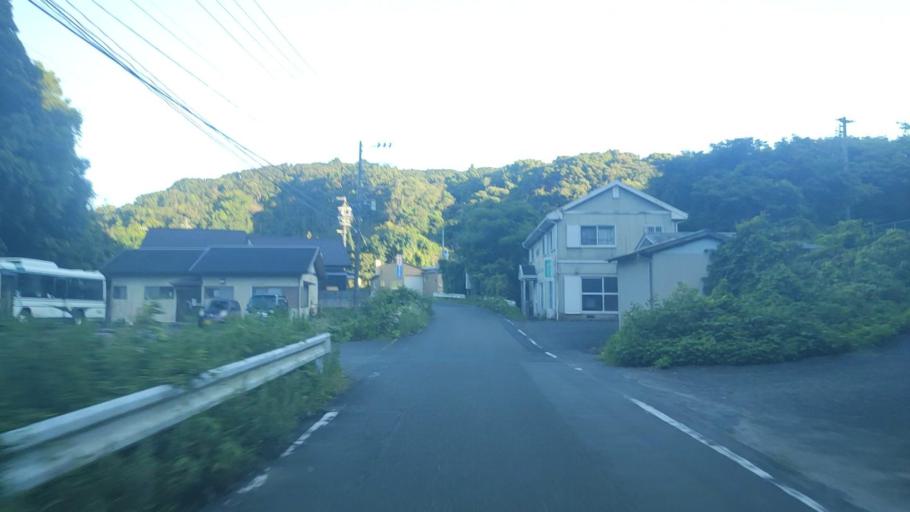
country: JP
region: Mie
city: Ise
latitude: 34.2705
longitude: 136.7665
